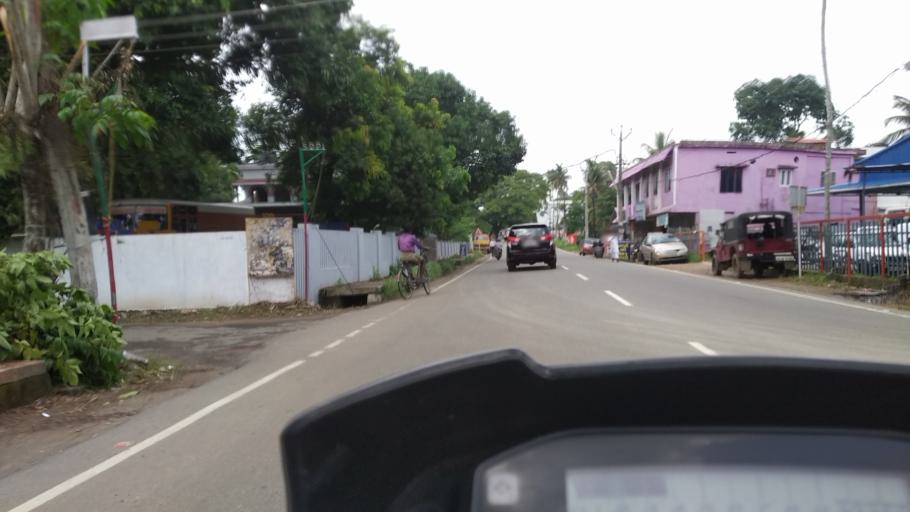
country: IN
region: Kerala
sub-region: Ernakulam
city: Aluva
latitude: 10.1261
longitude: 76.3155
